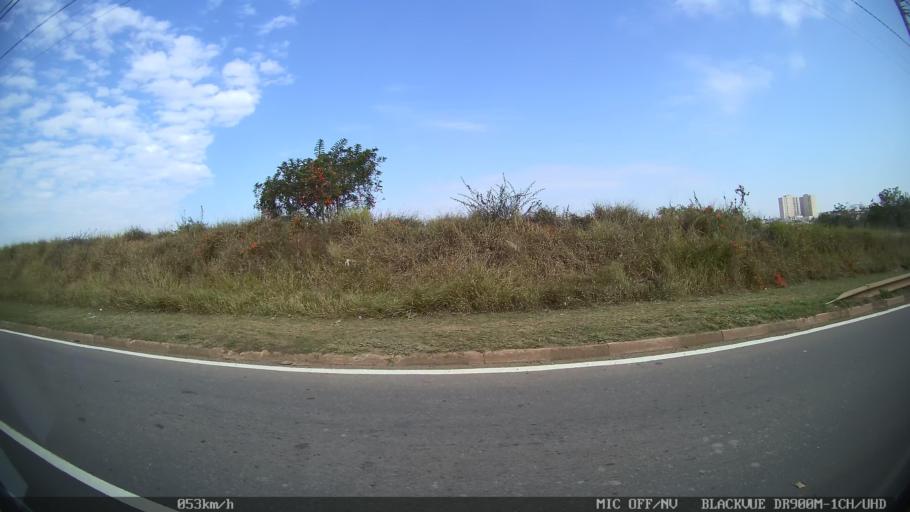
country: BR
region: Sao Paulo
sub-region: Paulinia
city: Paulinia
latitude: -22.7854
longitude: -47.1732
